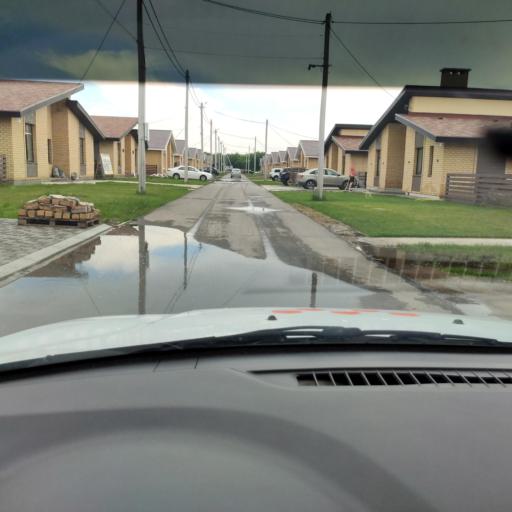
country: RU
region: Samara
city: Podstepki
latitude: 53.5747
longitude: 49.0871
